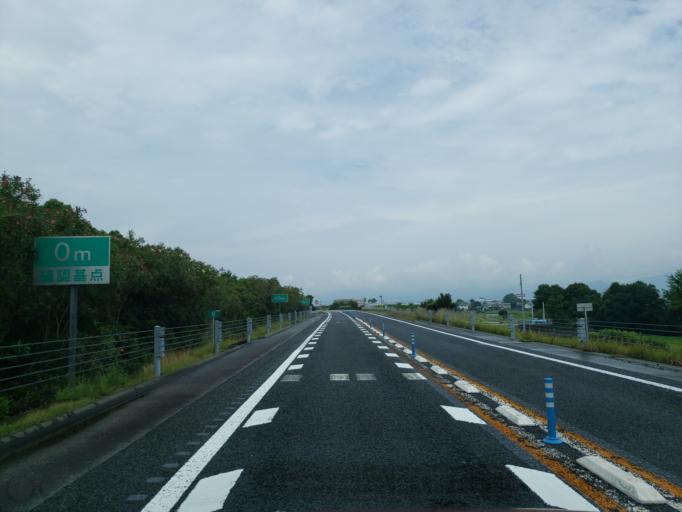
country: JP
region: Tokushima
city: Tokushima-shi
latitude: 34.1100
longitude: 134.5119
